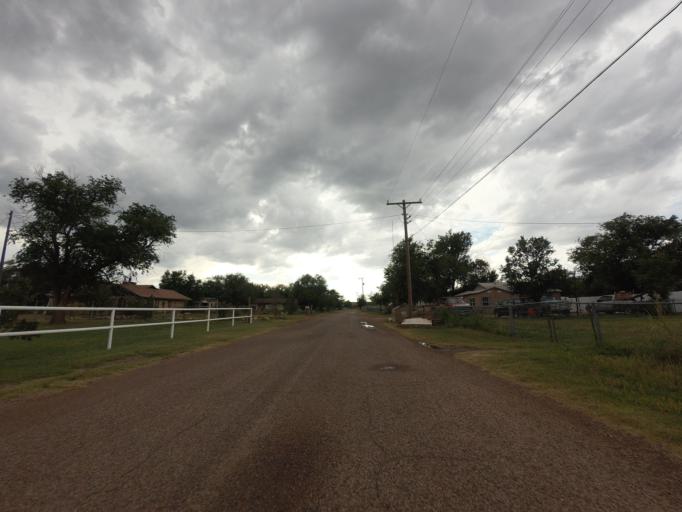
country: US
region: New Mexico
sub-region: Curry County
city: Clovis
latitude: 34.3881
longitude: -103.1828
